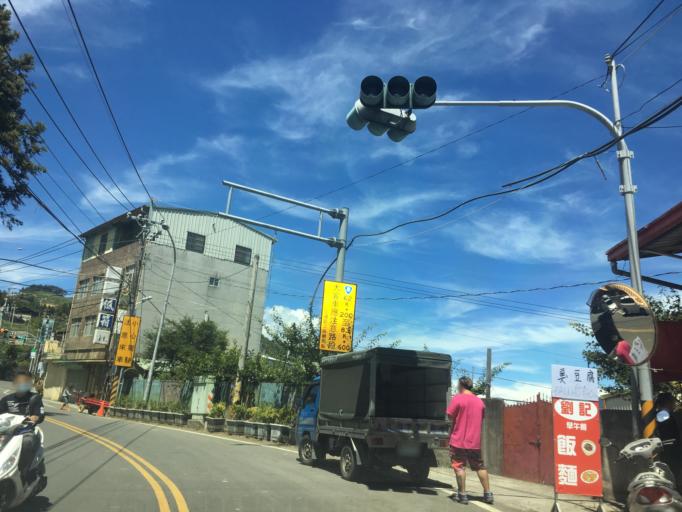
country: TW
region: Taiwan
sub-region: Nantou
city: Puli
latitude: 24.2580
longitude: 121.2619
